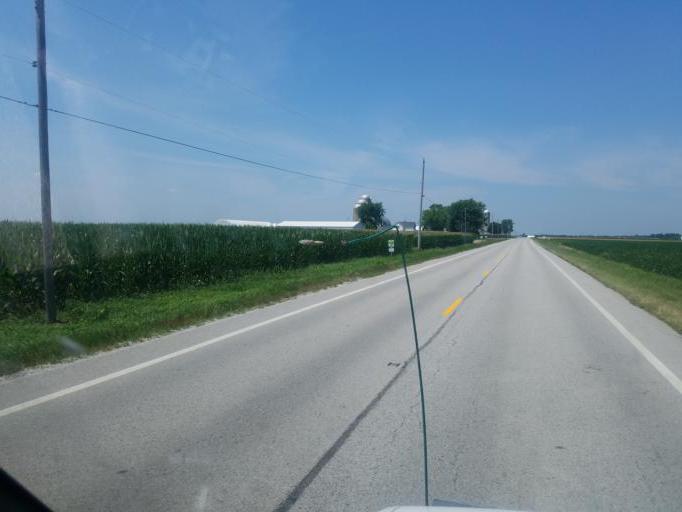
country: US
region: Ohio
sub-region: Auglaize County
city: New Bremen
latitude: 40.4547
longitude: -84.4341
